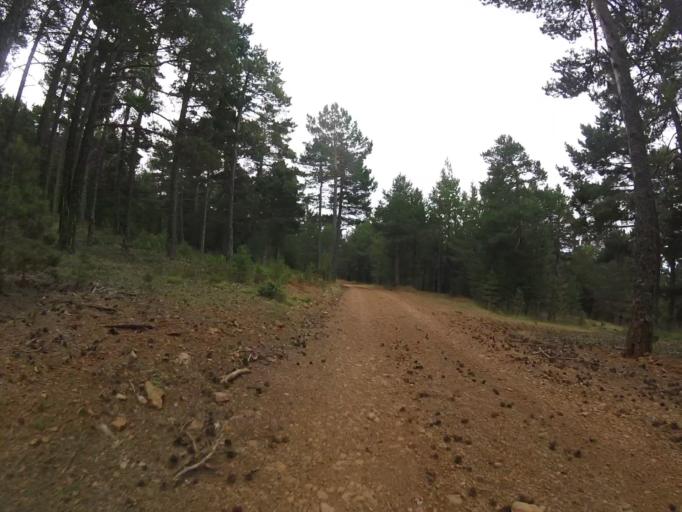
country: ES
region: Aragon
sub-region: Provincia de Teruel
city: Valdelinares
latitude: 40.3669
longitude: -0.6185
